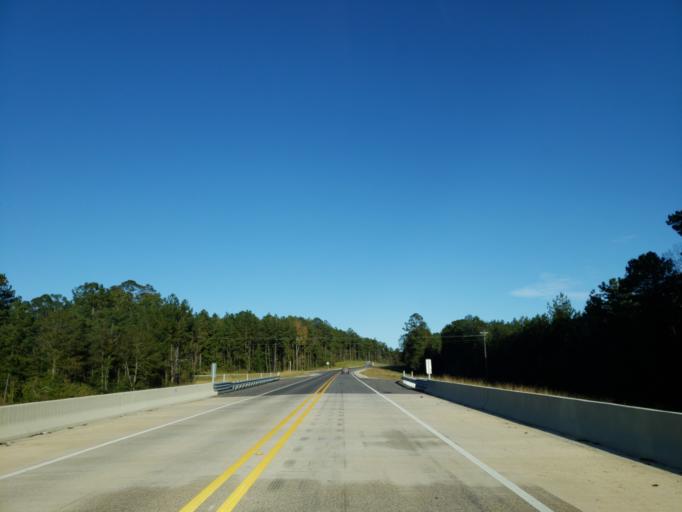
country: US
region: Mississippi
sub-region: Perry County
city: Richton
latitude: 31.3738
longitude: -88.8412
